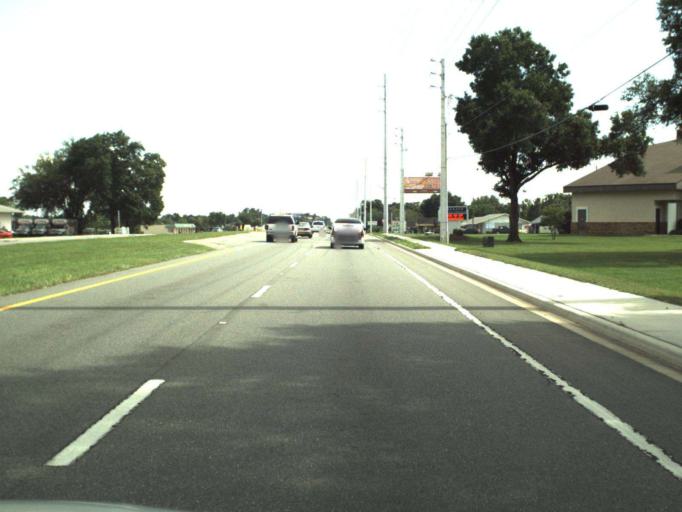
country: US
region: Florida
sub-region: Marion County
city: Silver Springs Shores
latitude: 29.1745
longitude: -82.0538
